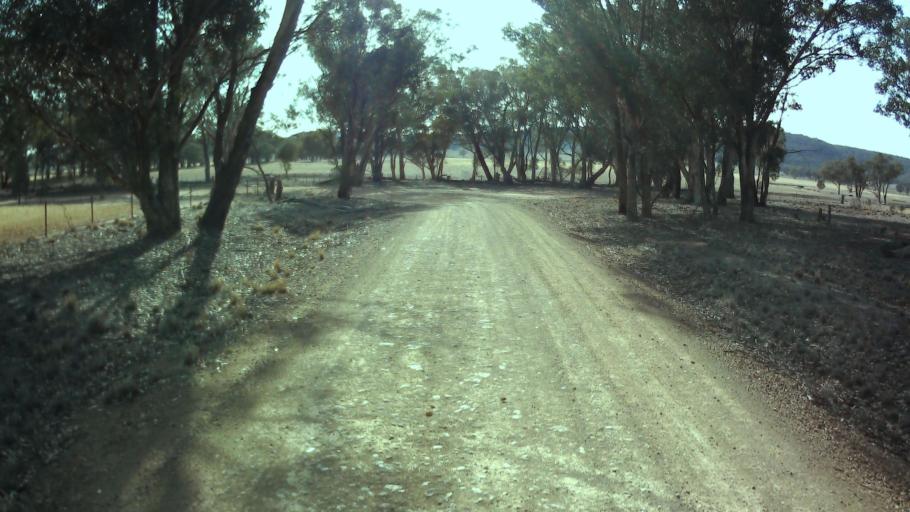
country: AU
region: New South Wales
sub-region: Weddin
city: Grenfell
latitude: -33.7978
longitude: 148.0928
